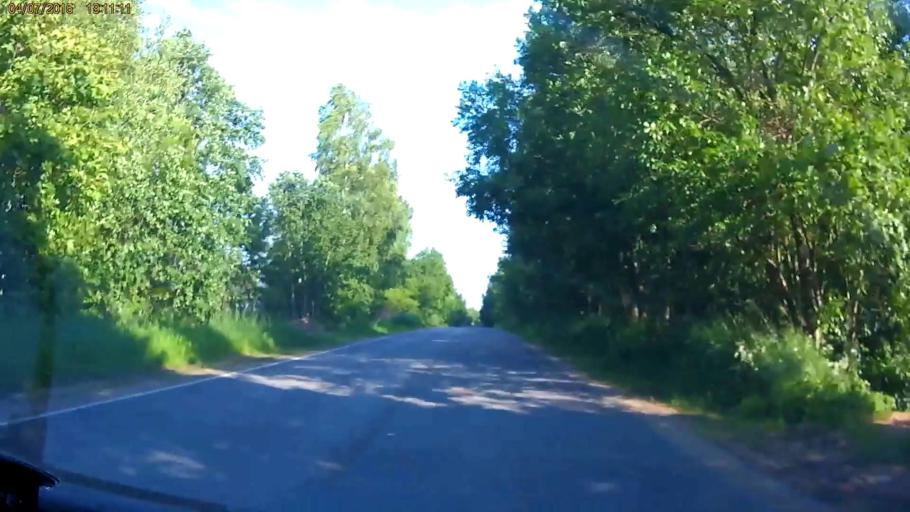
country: RU
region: Leningrad
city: Garbolovo
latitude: 60.3306
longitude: 30.4904
